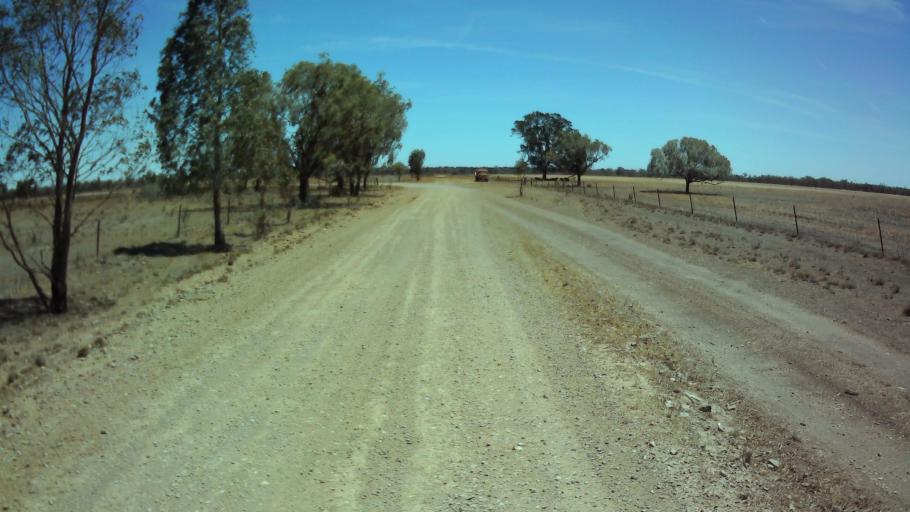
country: AU
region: New South Wales
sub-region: Bland
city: West Wyalong
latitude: -33.8227
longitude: 147.6431
